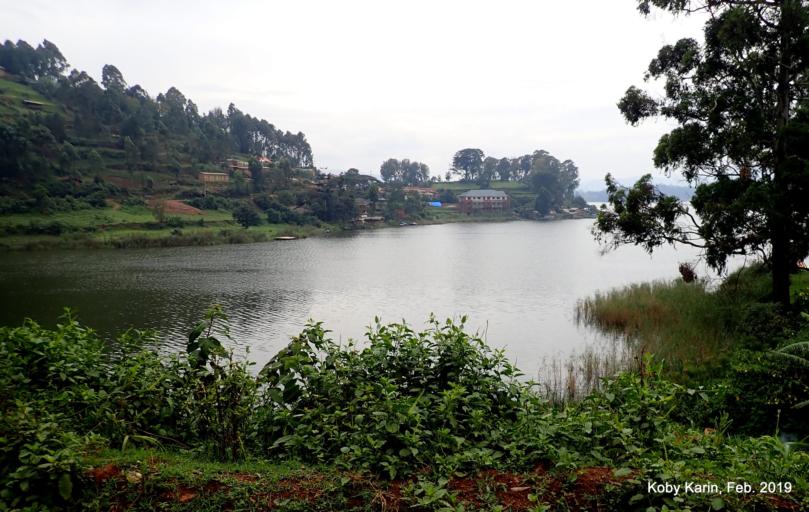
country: UG
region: Western Region
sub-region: Kabale District
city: Kabale
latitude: -1.2652
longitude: 29.9383
